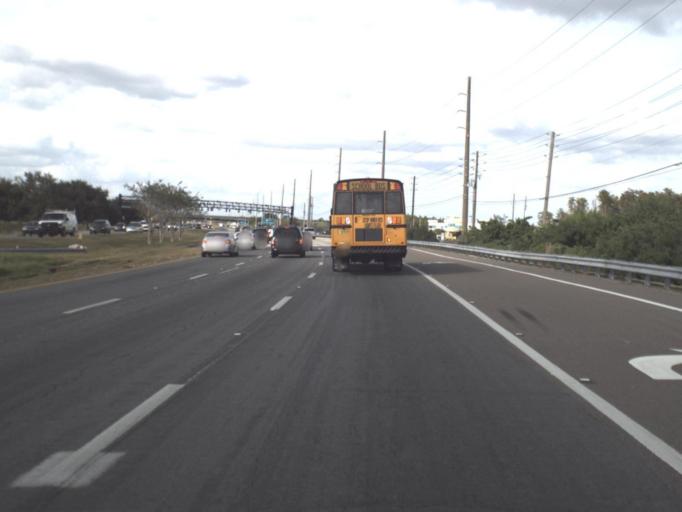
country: US
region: Florida
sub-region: Orange County
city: Williamsburg
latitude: 28.4138
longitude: -81.4228
